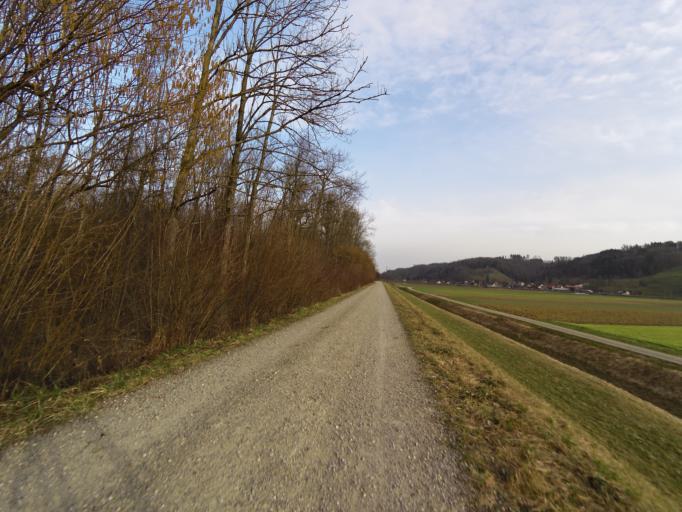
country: CH
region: Thurgau
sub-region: Frauenfeld District
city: Mullheim
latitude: 47.5853
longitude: 8.9961
